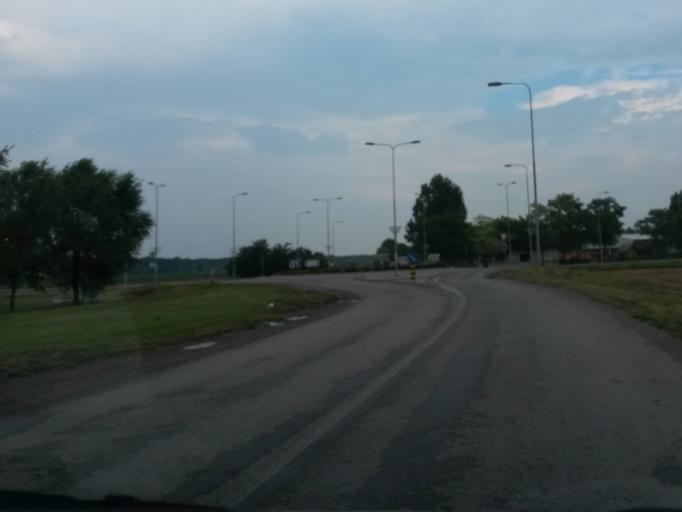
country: RS
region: Autonomna Pokrajina Vojvodina
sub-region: Zapadnobacki Okrug
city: Apatin
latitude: 45.6701
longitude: 19.0297
